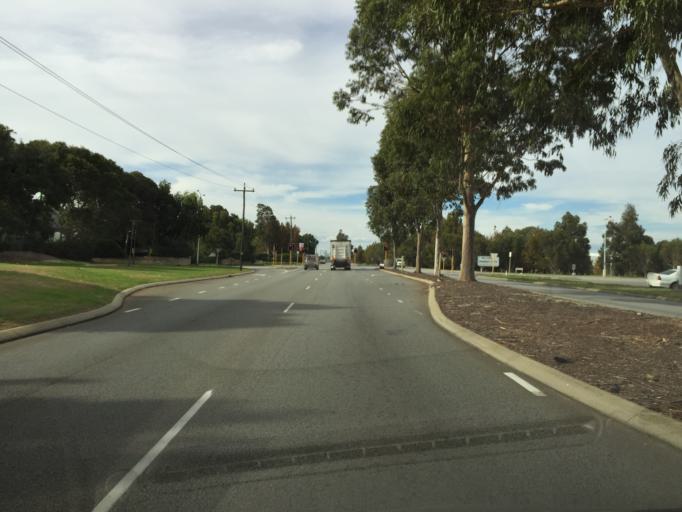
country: AU
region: Western Australia
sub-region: Canning
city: Willetton
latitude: -32.0702
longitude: 115.8951
